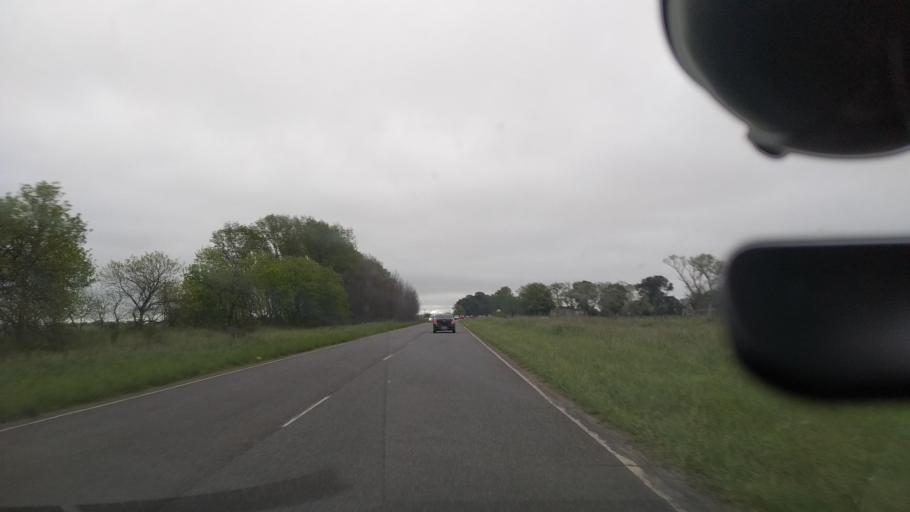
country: AR
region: Buenos Aires
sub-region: Partido de Magdalena
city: Magdalena
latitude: -35.2008
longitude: -57.7777
